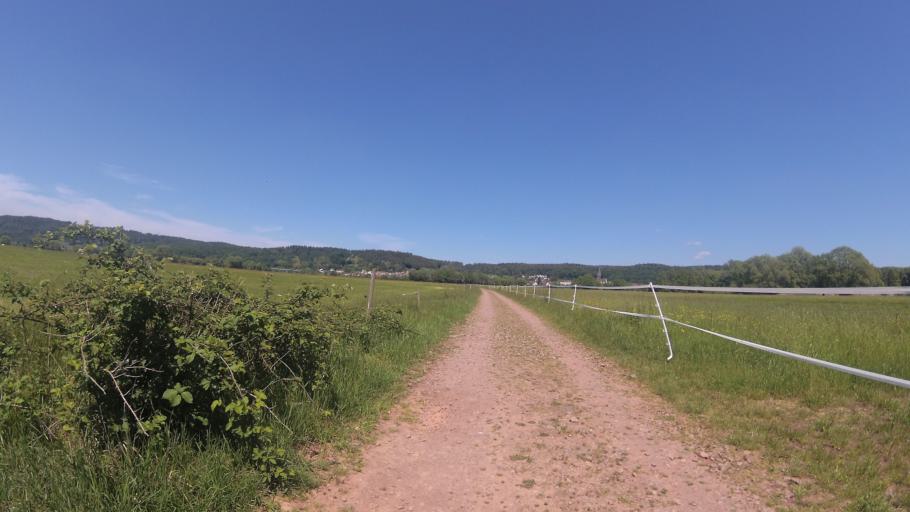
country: DE
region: Saarland
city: Mettlach
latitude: 49.4680
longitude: 6.5990
